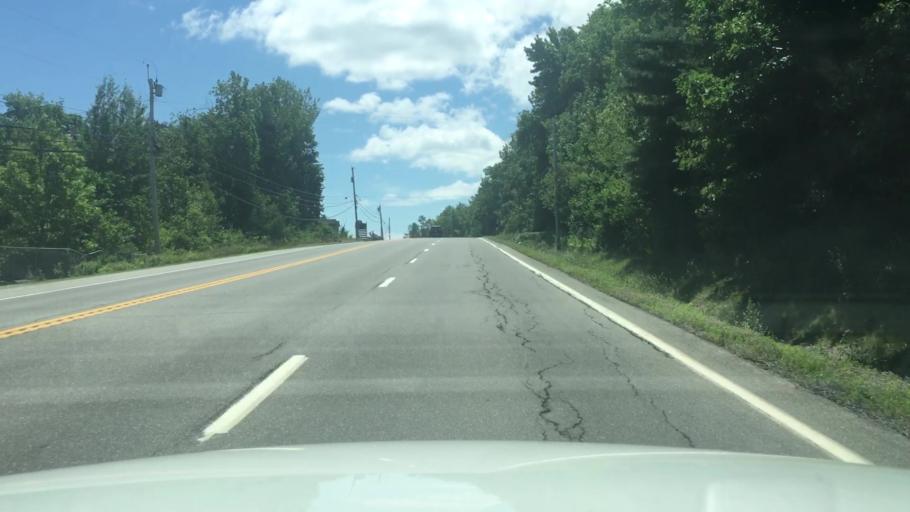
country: US
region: Maine
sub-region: Waldo County
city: Northport
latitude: 44.3627
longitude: -68.9768
